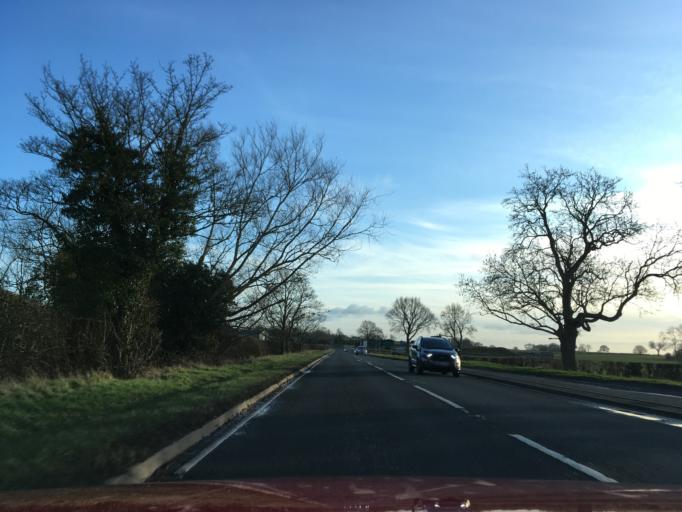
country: GB
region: England
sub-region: Warwickshire
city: Henley in Arden
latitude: 52.2433
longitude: -1.7472
